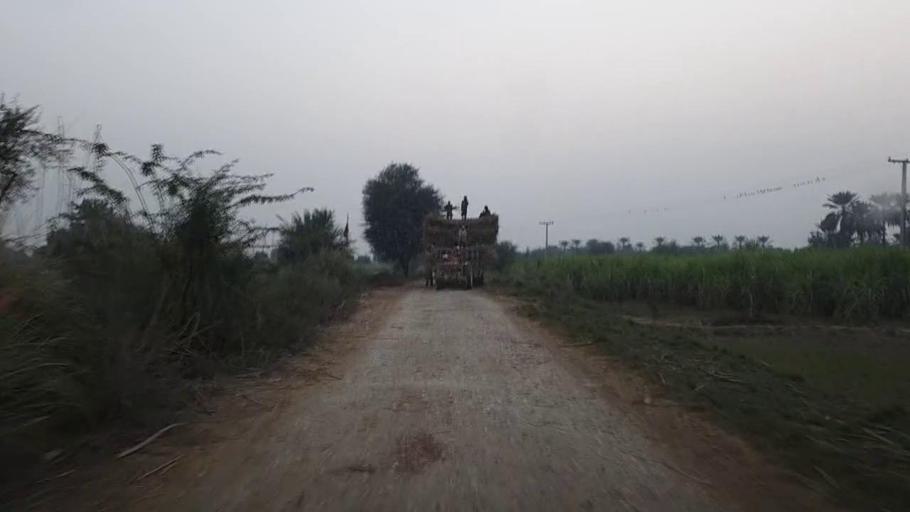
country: PK
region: Sindh
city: Karaundi
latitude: 26.9468
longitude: 68.4474
